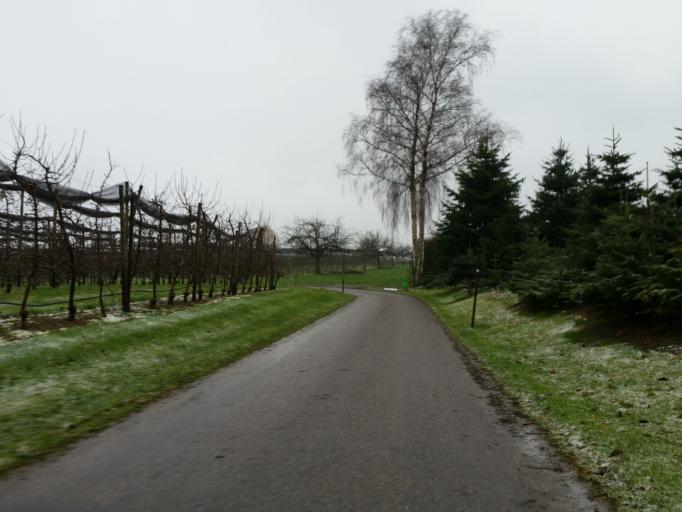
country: CH
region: Thurgau
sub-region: Arbon District
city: Egnach
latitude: 47.5286
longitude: 9.3841
